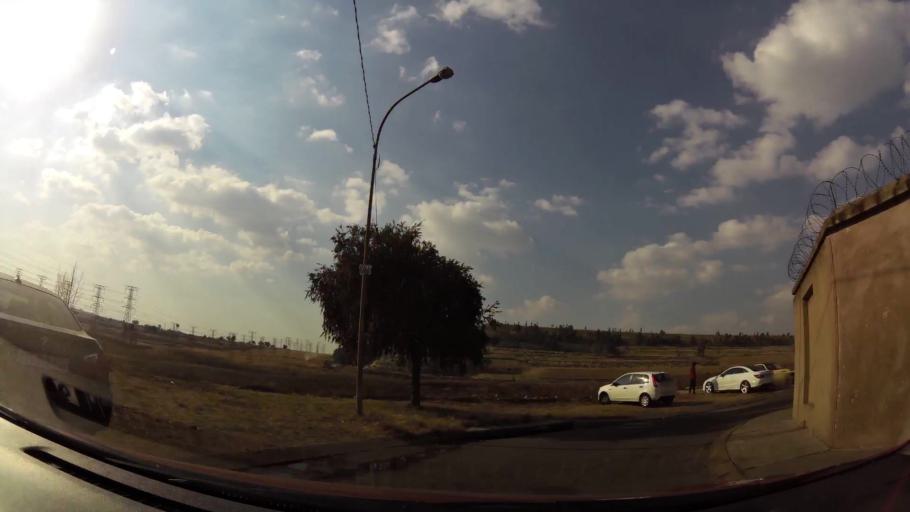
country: ZA
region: Gauteng
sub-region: City of Johannesburg Metropolitan Municipality
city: Soweto
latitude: -26.2324
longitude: 27.9444
